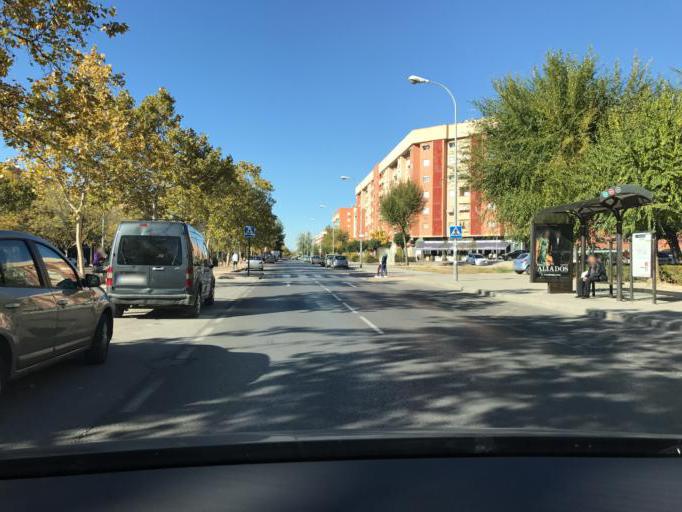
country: ES
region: Andalusia
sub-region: Provincia de Granada
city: Granada
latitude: 37.2017
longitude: -3.6092
